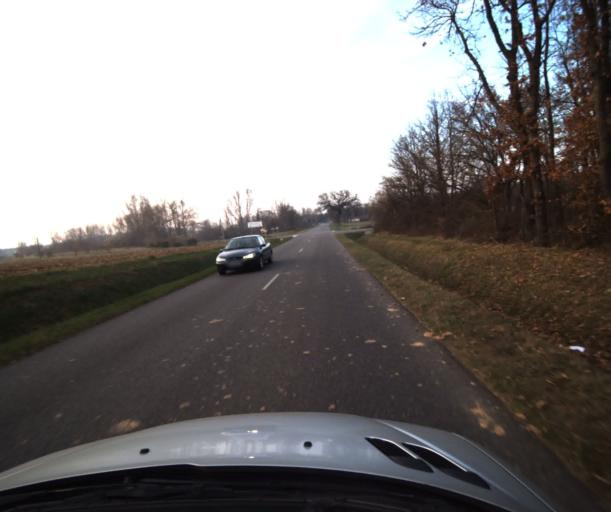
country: FR
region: Midi-Pyrenees
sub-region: Departement du Tarn-et-Garonne
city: Labastide-Saint-Pierre
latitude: 43.8998
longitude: 1.3702
